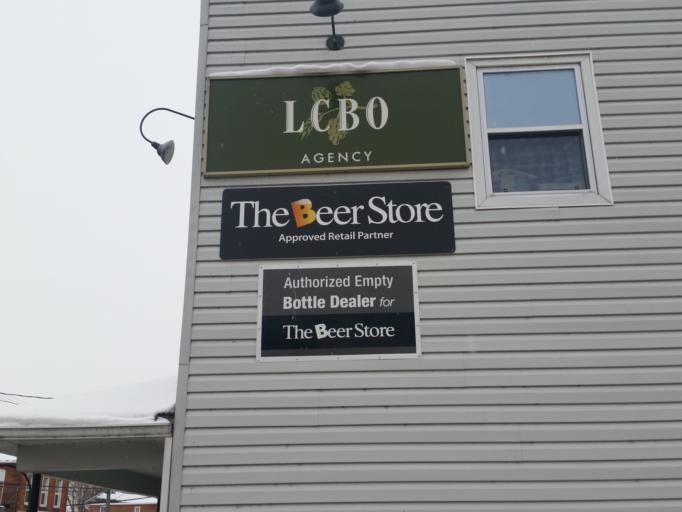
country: CA
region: Ontario
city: Arnprior
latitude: 45.3337
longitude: -76.2905
